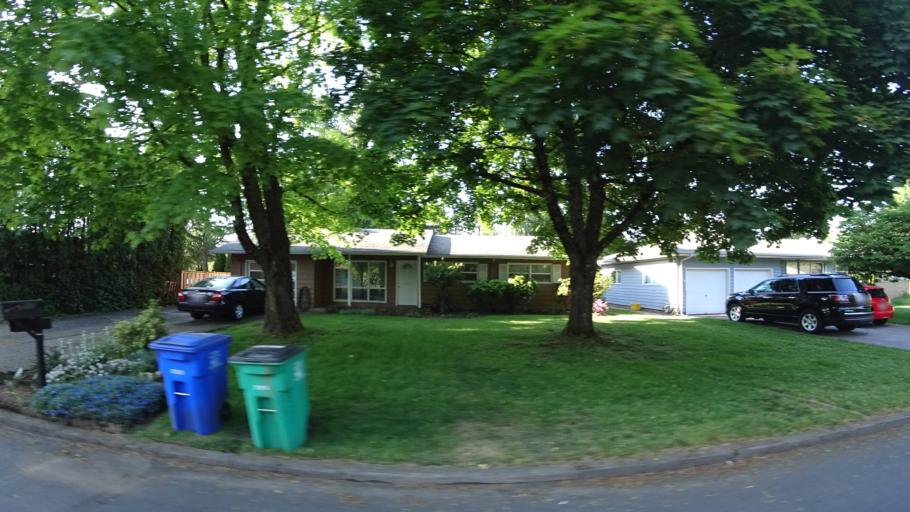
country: US
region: Oregon
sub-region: Multnomah County
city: Gresham
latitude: 45.5105
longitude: -122.4956
